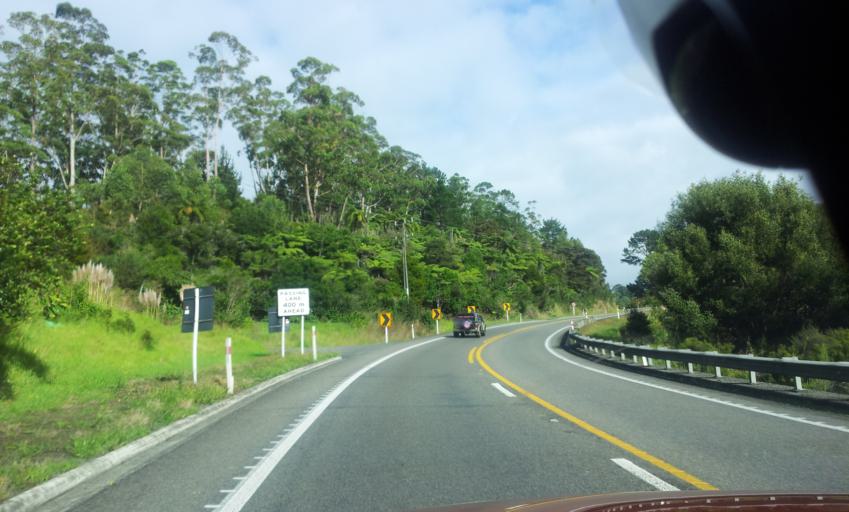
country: NZ
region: Auckland
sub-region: Auckland
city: Warkworth
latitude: -36.3685
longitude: 174.6236
